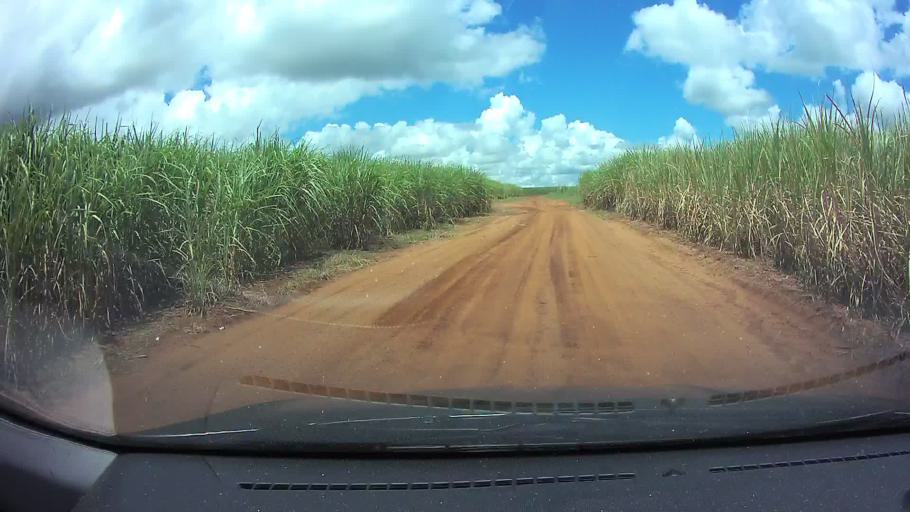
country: PY
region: Paraguari
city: La Colmena
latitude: -25.9637
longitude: -56.7628
